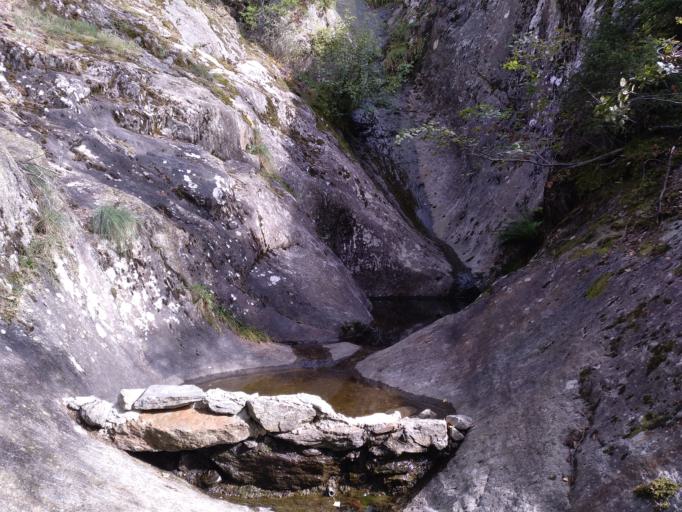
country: FR
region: Rhone-Alpes
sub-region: Departement de la Haute-Savoie
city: Chamonix-Mont-Blanc
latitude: 45.9410
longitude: 6.9107
